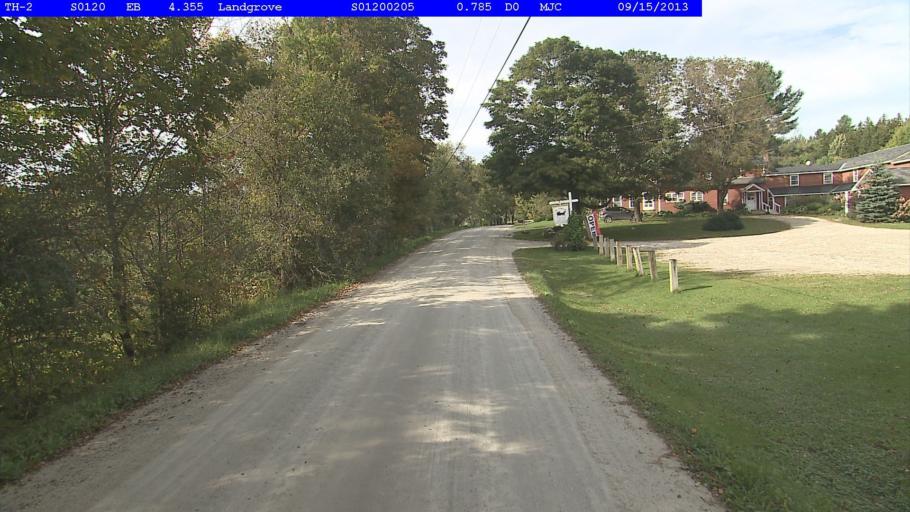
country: US
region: Vermont
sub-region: Bennington County
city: Manchester Center
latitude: 43.2711
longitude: -72.8613
